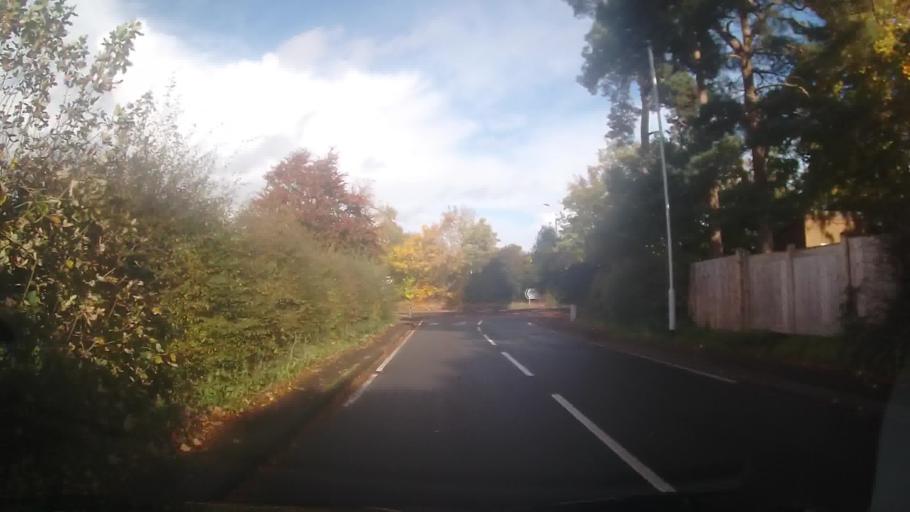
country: GB
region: England
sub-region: Shropshire
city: Whitchurch
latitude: 52.9614
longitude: -2.6783
